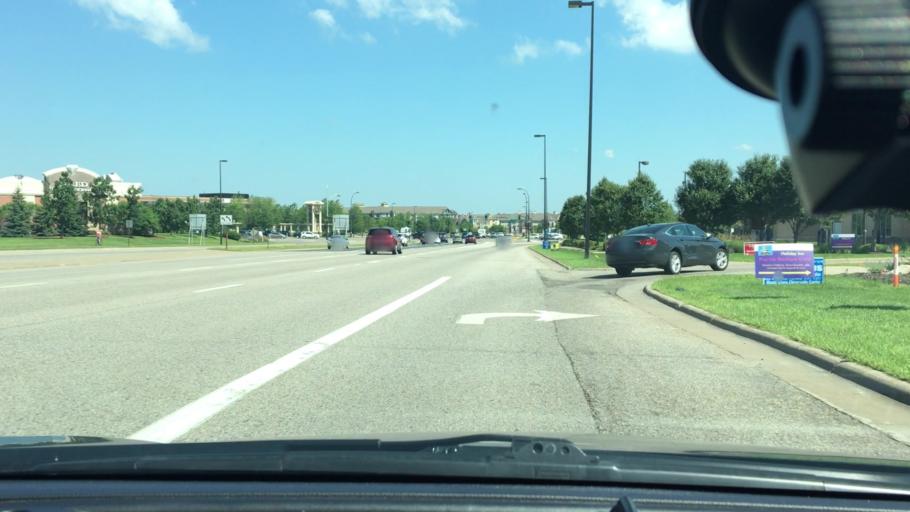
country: US
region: Minnesota
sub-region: Hennepin County
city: Maple Grove
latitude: 45.0926
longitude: -93.4313
